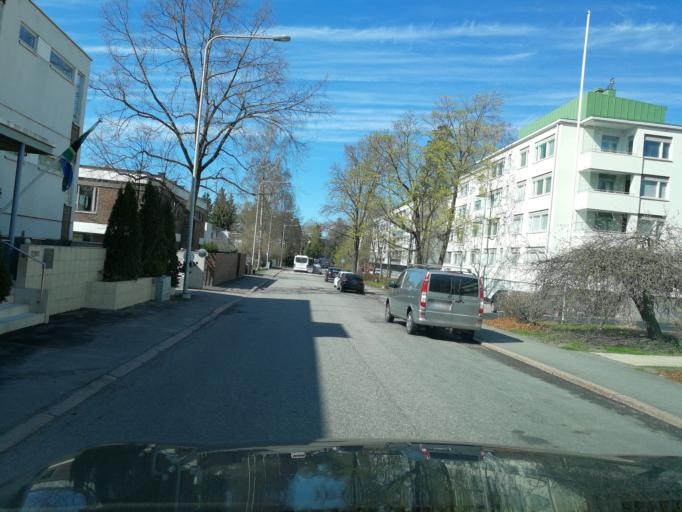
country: FI
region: Uusimaa
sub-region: Helsinki
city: Teekkarikylae
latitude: 60.1666
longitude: 24.8579
